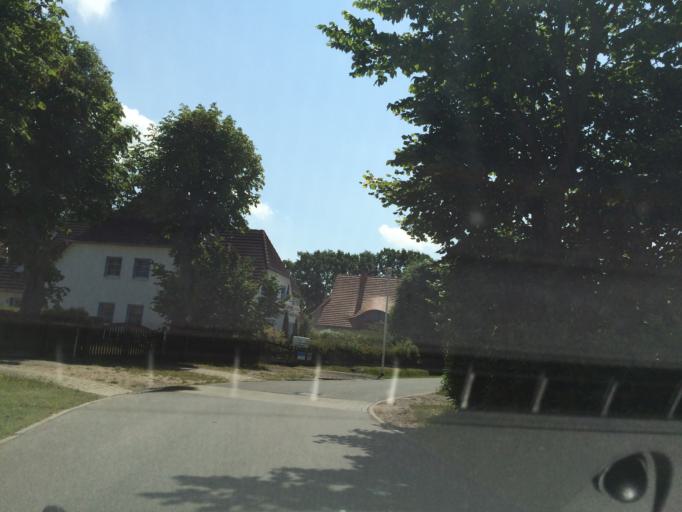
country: DE
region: Mecklenburg-Vorpommern
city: Zingst
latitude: 54.4335
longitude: 12.6808
